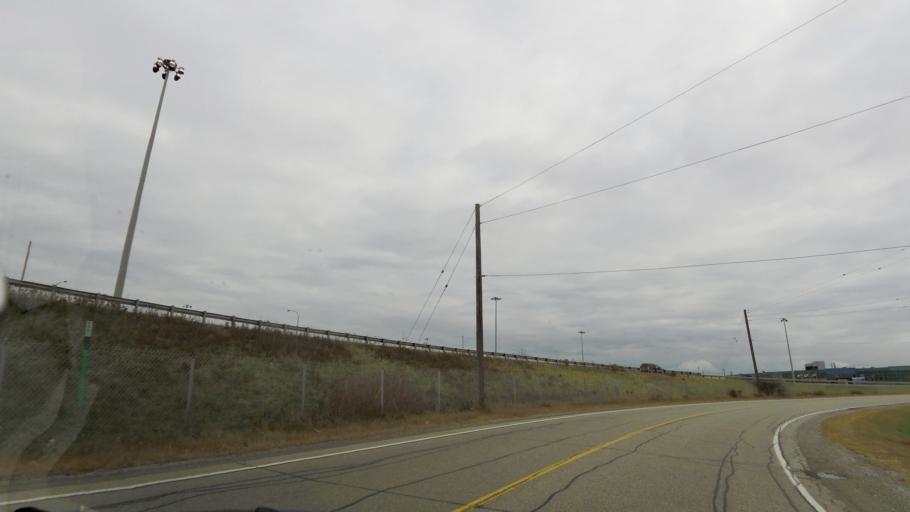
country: CA
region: Ontario
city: Burlington
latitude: 43.3814
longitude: -79.7741
